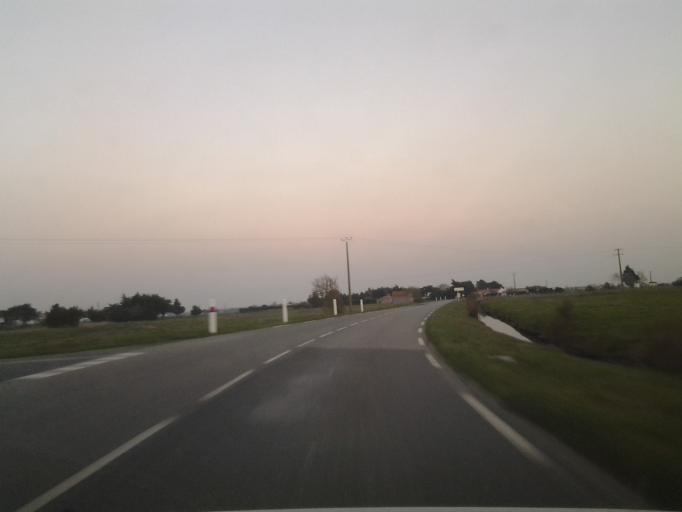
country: FR
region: Pays de la Loire
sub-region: Departement de la Vendee
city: Beauvoir-sur-Mer
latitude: 46.9207
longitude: -2.0859
